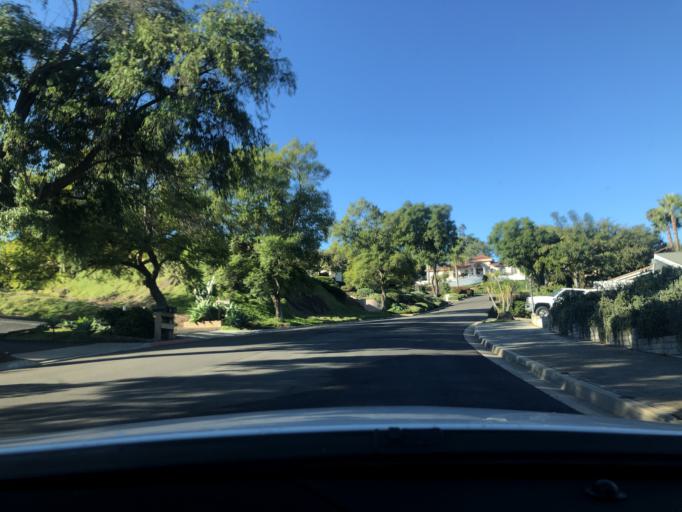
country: US
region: California
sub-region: San Diego County
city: Casa de Oro-Mount Helix
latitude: 32.7697
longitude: -116.9600
